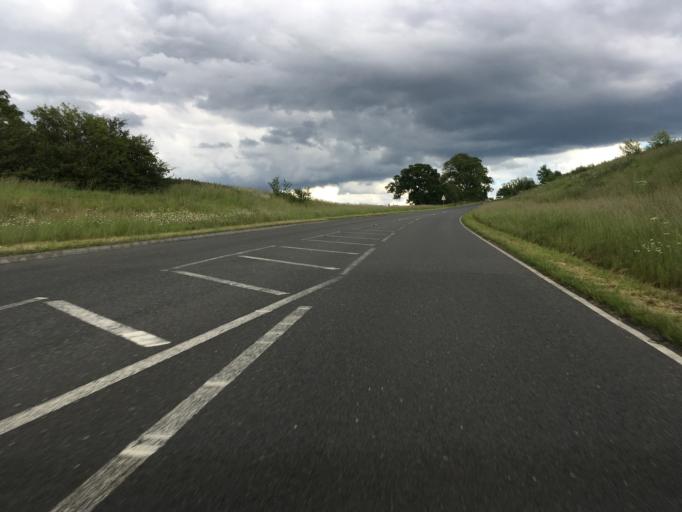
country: GB
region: England
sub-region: Central Bedfordshire
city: Leighton Buzzard
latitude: 51.9340
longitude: -0.6932
